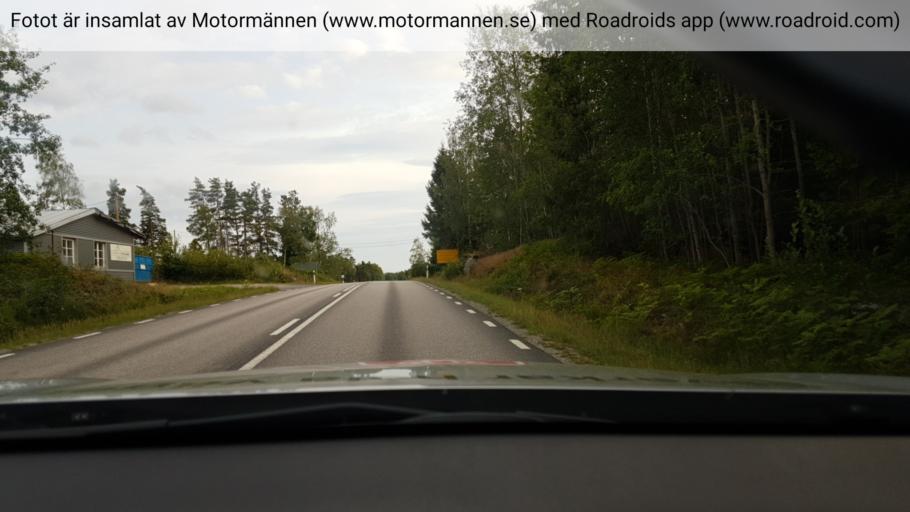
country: SE
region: Vaestra Goetaland
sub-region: Uddevalla Kommun
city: Uddevalla
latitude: 58.4257
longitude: 12.0195
